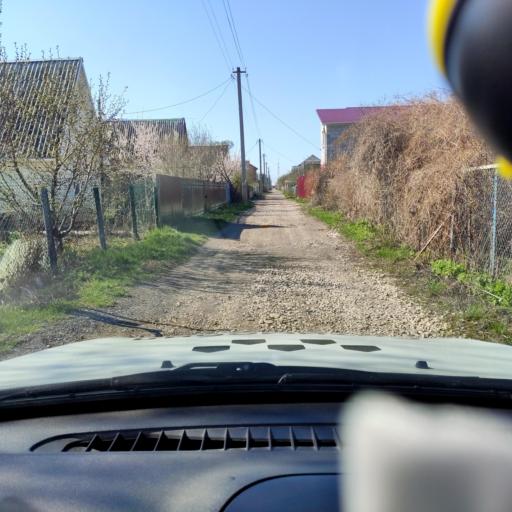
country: RU
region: Samara
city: Tol'yatti
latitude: 53.5969
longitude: 49.2946
